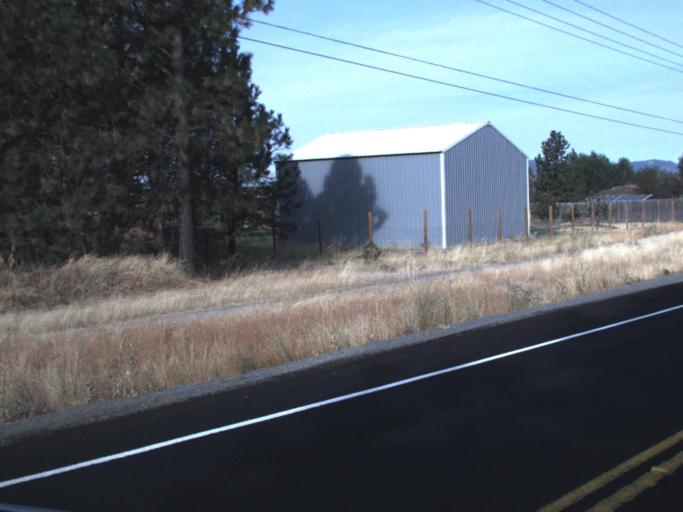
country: US
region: Washington
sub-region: Spokane County
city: Deer Park
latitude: 47.8271
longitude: -117.5954
